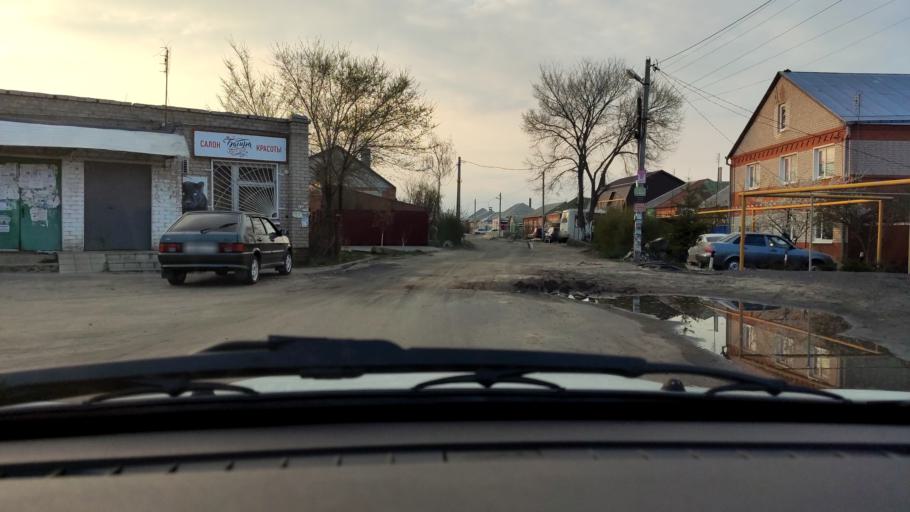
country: RU
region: Voronezj
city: Somovo
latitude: 51.7489
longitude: 39.3352
